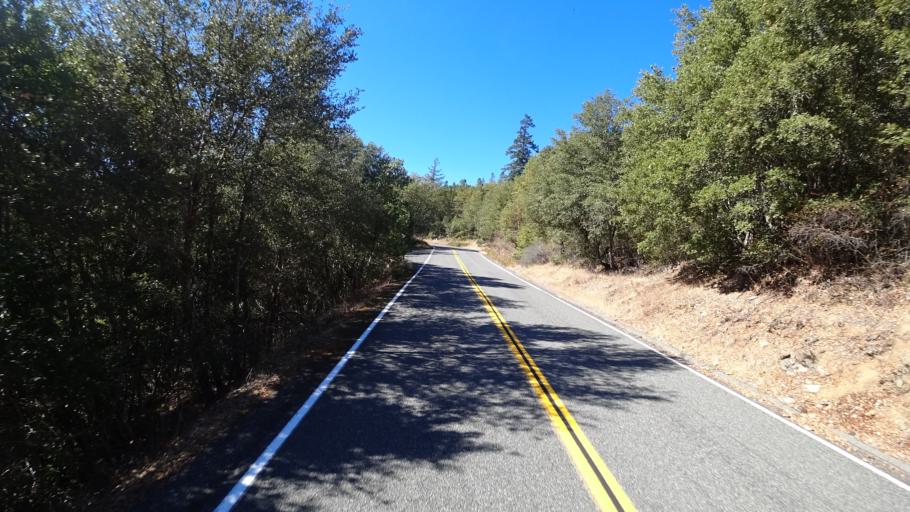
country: US
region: California
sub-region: Siskiyou County
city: Happy Camp
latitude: 41.3797
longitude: -123.4838
